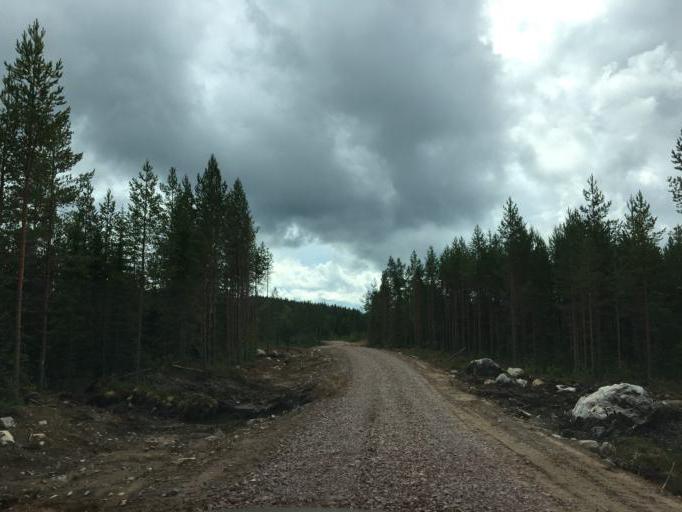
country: SE
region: OErebro
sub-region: Hallefors Kommun
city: Haellefors
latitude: 60.0738
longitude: 14.4749
